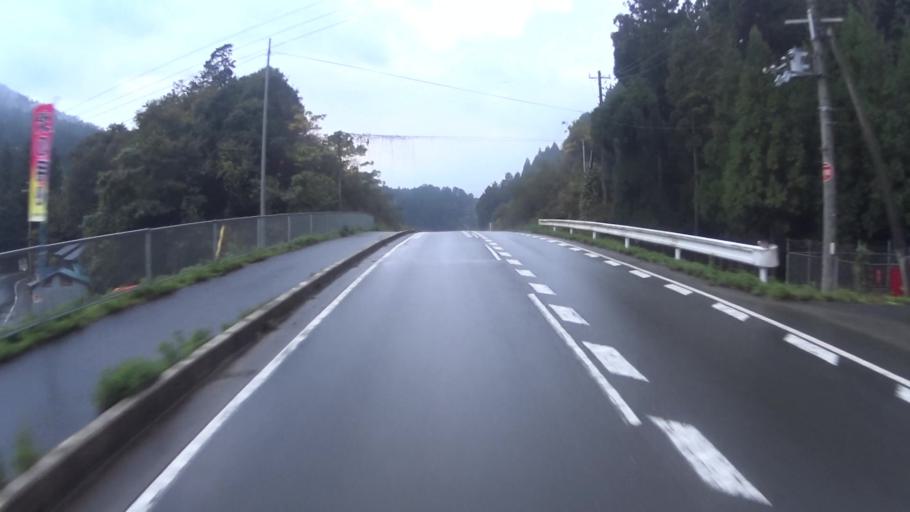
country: JP
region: Kyoto
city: Miyazu
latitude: 35.4549
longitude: 135.2172
